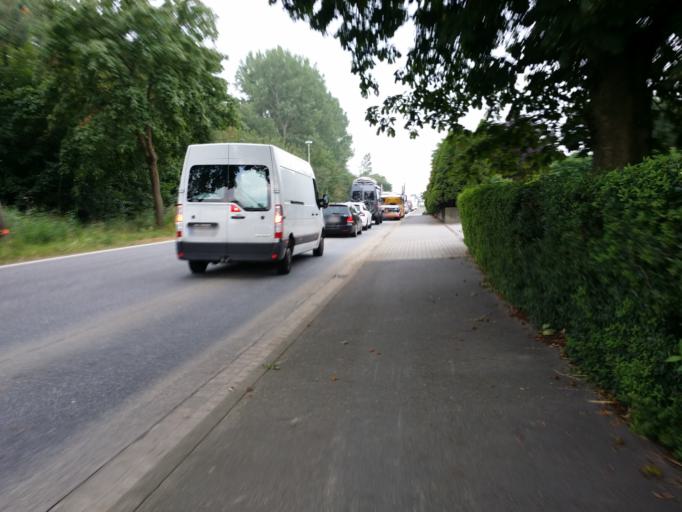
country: DE
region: Schleswig-Holstein
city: Blomesche Wildnis
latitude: 53.8079
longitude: 9.4202
